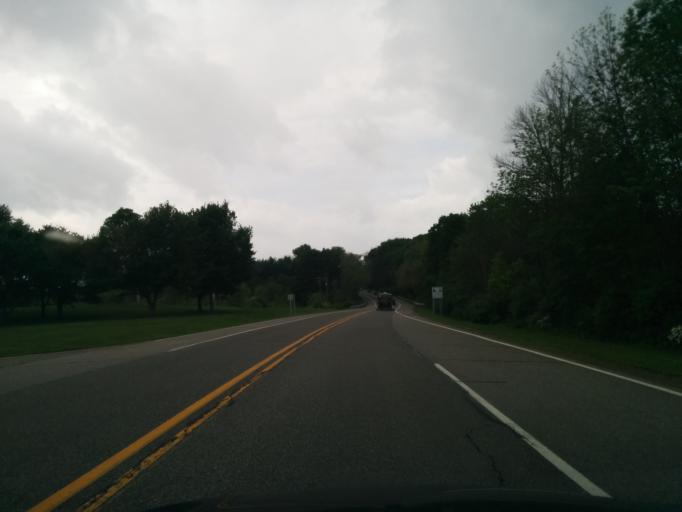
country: US
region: Michigan
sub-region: Berrien County
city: Benton Harbor
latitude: 42.1506
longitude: -86.4449
